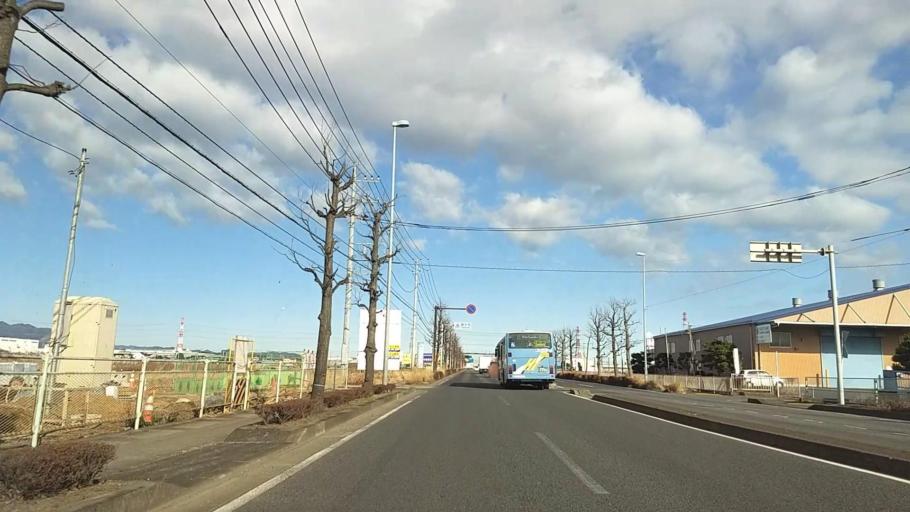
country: JP
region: Kanagawa
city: Atsugi
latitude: 35.3945
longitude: 139.3616
